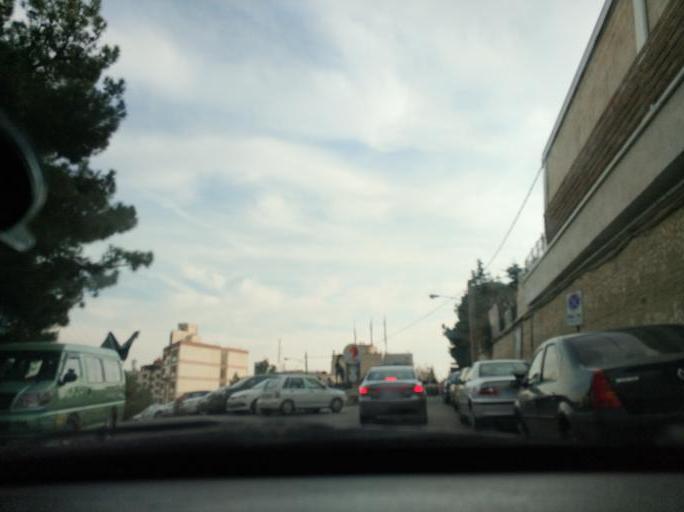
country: IR
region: Tehran
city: Tajrish
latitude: 35.8156
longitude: 51.4874
